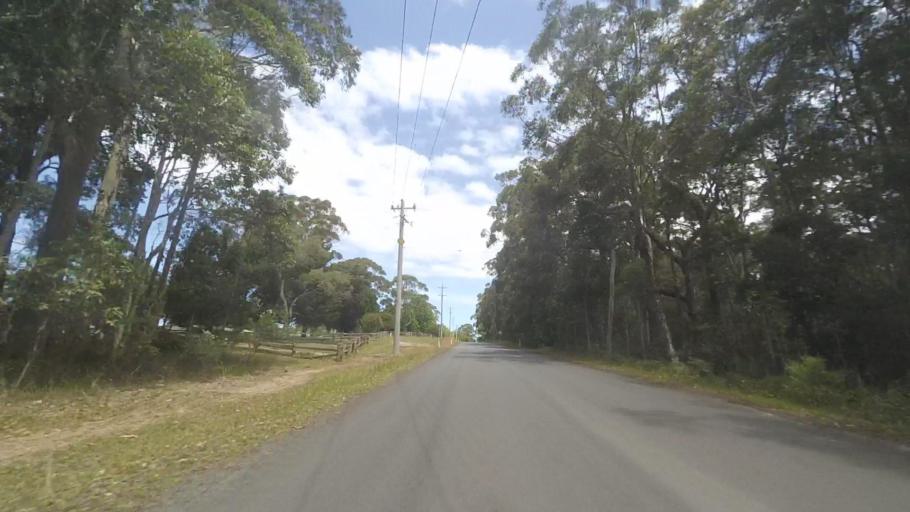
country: AU
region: New South Wales
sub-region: Shoalhaven Shire
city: Milton
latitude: -35.3942
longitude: 150.3690
